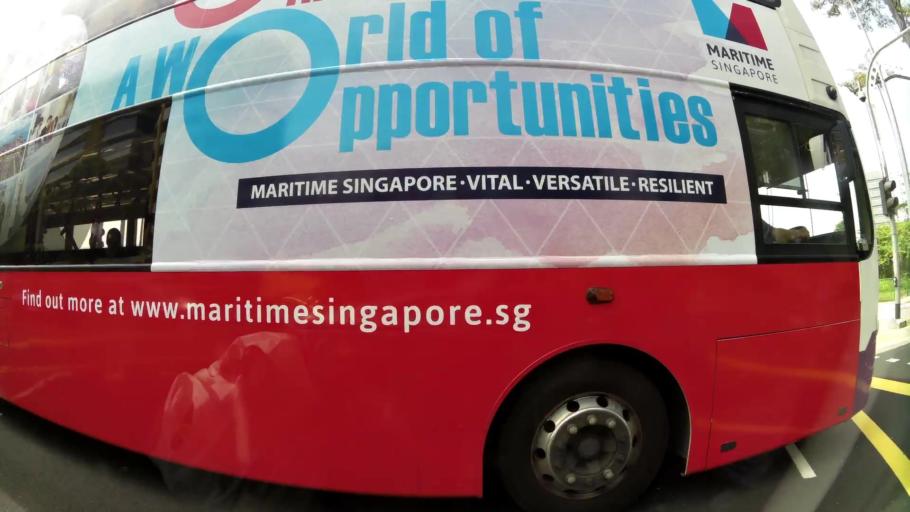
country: SG
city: Singapore
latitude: 1.3275
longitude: 103.7519
